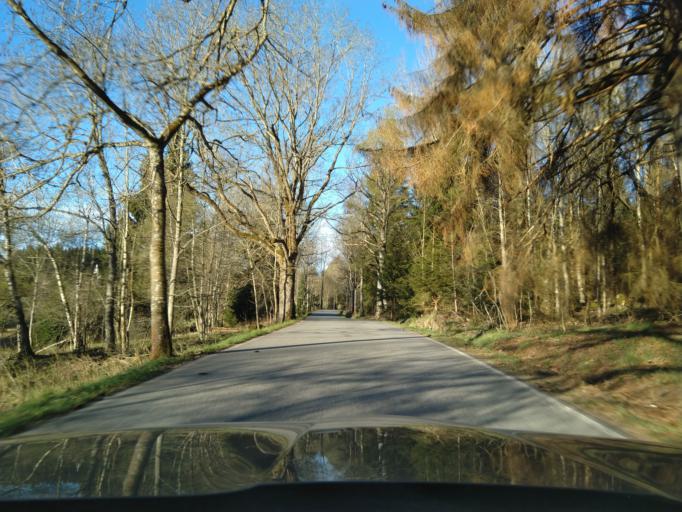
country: DE
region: Bavaria
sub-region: Lower Bavaria
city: Haidmuhle
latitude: 48.8859
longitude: 13.7864
